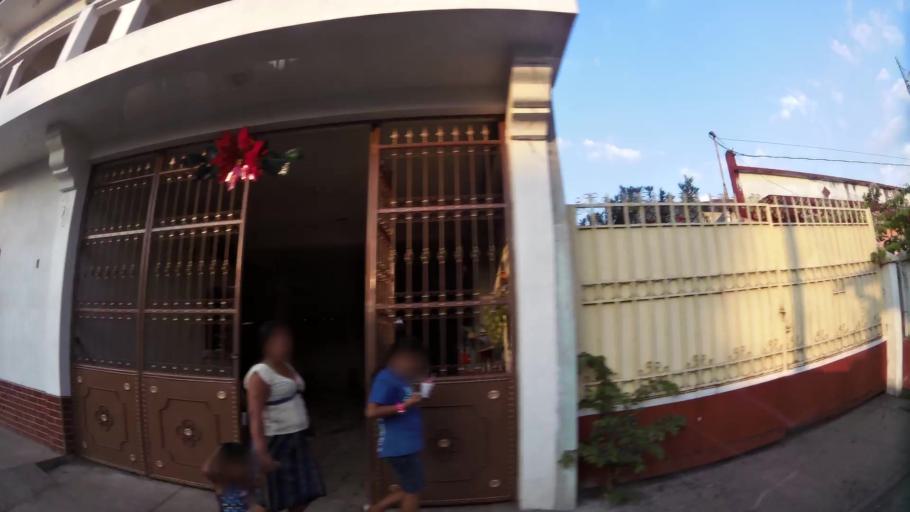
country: GT
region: Retalhuleu
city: San Sebastian
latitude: 14.5620
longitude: -91.6513
